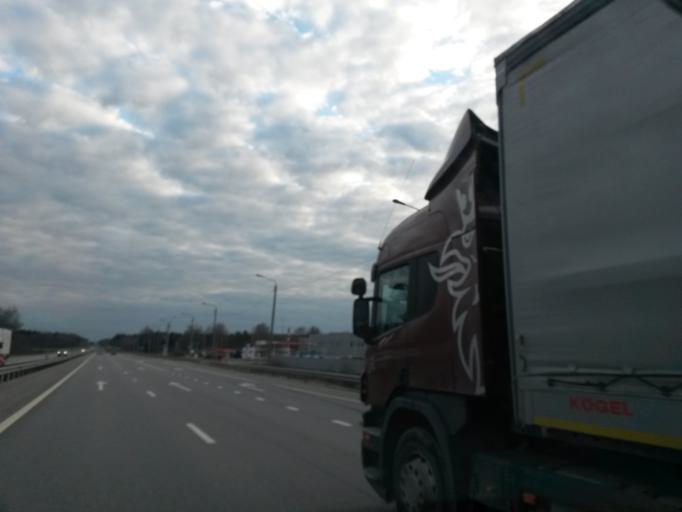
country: RU
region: Moskovskaya
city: Ashukino
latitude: 56.1365
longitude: 38.0012
